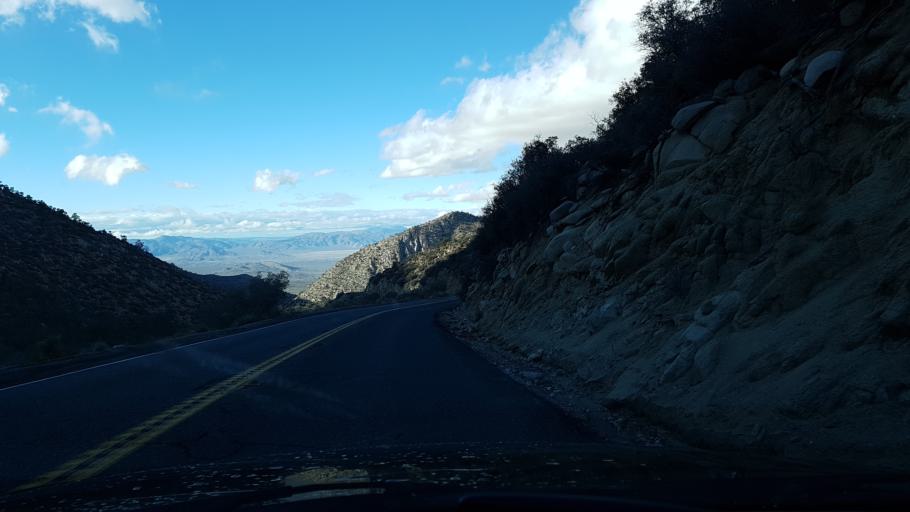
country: US
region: California
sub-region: San Bernardino County
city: Big Bear City
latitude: 34.3284
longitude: -116.8276
